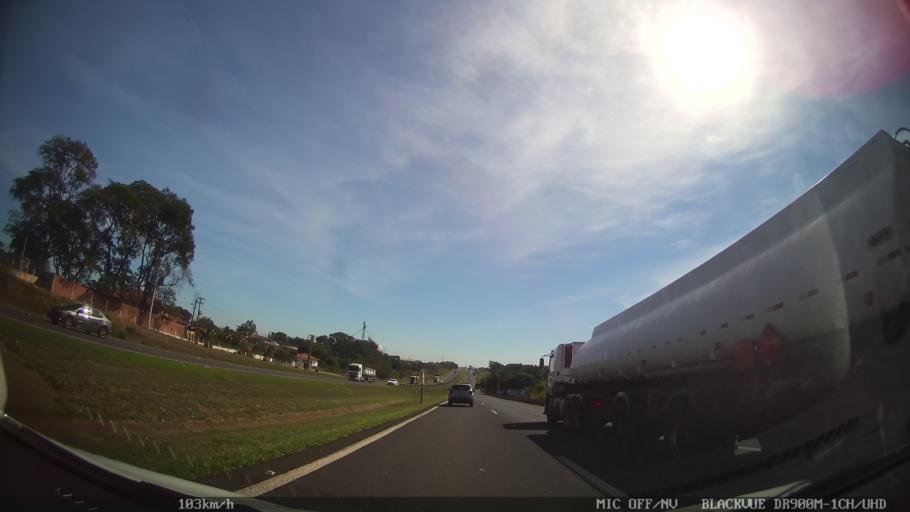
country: BR
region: Sao Paulo
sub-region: Pirassununga
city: Pirassununga
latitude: -22.0270
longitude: -47.4357
